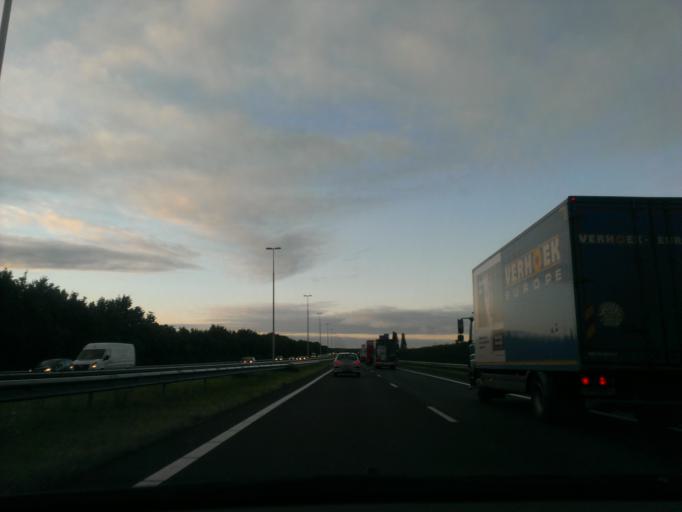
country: NL
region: Gelderland
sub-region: Gemeente Apeldoorn
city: Apeldoorn
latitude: 52.2264
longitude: 6.0180
